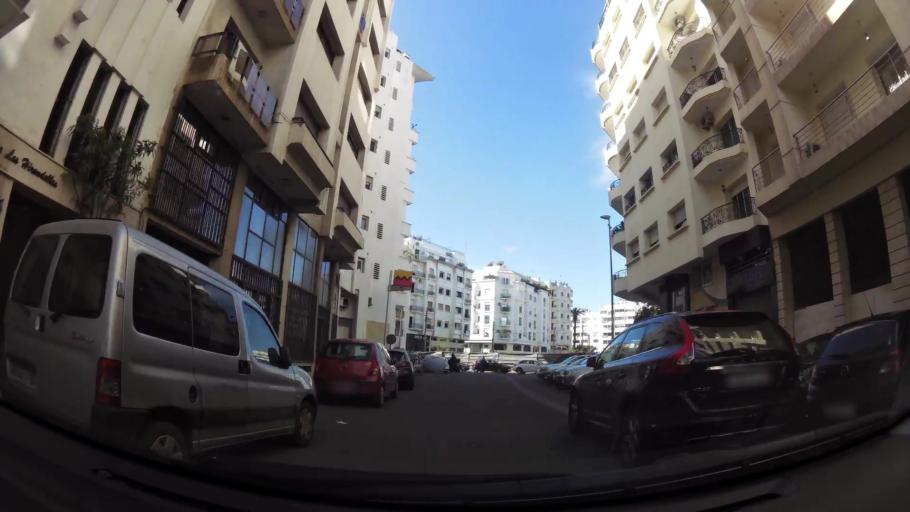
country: MA
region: Grand Casablanca
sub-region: Casablanca
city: Casablanca
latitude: 33.5899
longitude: -7.6364
